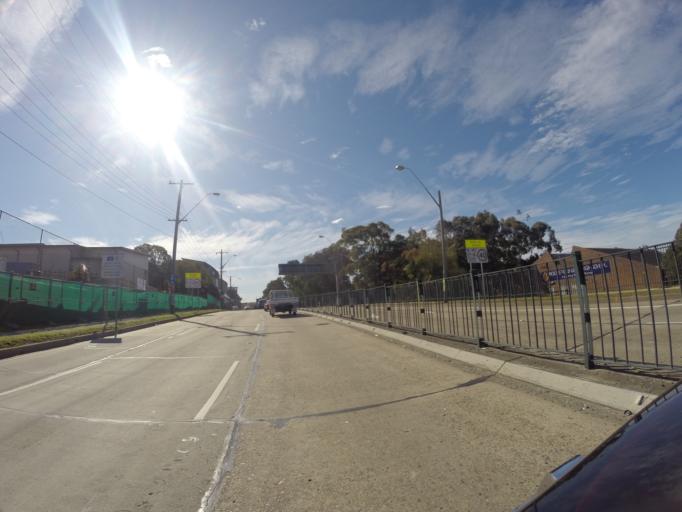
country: AU
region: New South Wales
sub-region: Kogarah
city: Beverly Park
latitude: -33.9687
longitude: 151.1362
